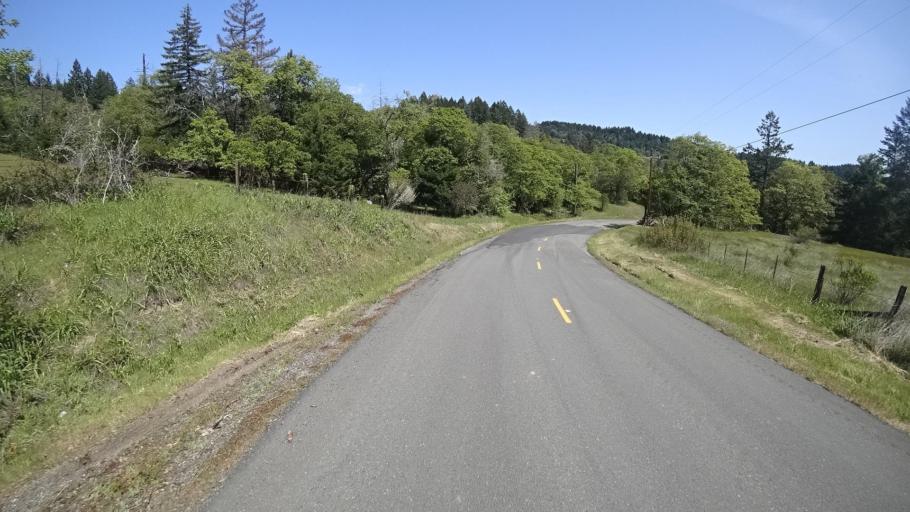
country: US
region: California
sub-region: Humboldt County
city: Redway
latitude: 40.2744
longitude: -123.6306
